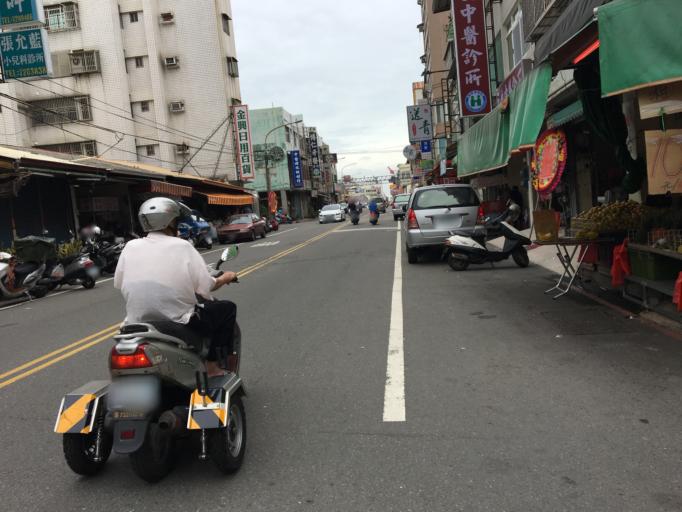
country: TW
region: Taiwan
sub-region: Changhua
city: Chang-hua
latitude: 24.0868
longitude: 120.5450
